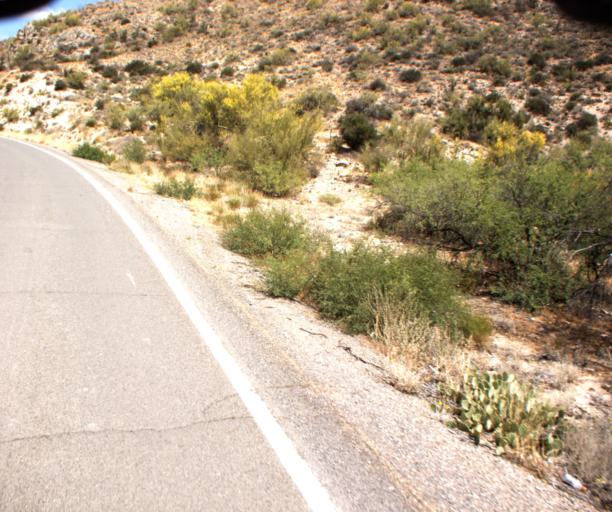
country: US
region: Arizona
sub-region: Pinal County
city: Superior
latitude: 33.2314
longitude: -111.0881
